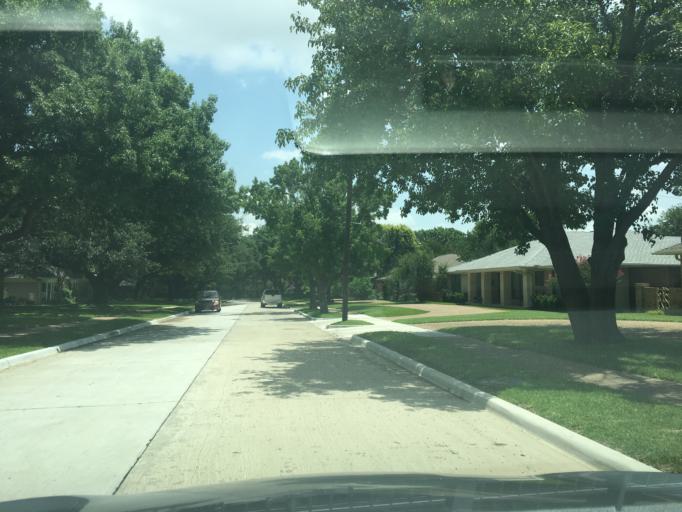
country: US
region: Texas
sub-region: Dallas County
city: University Park
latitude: 32.8843
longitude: -96.7795
